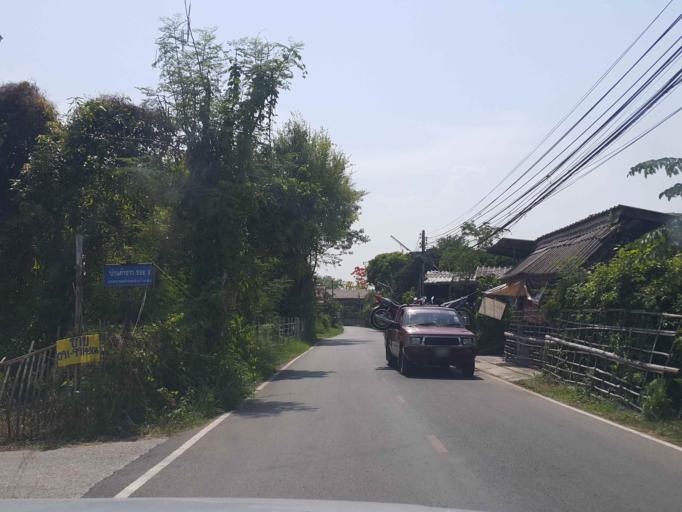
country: TH
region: Chiang Mai
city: San Kamphaeng
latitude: 18.7522
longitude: 99.1302
